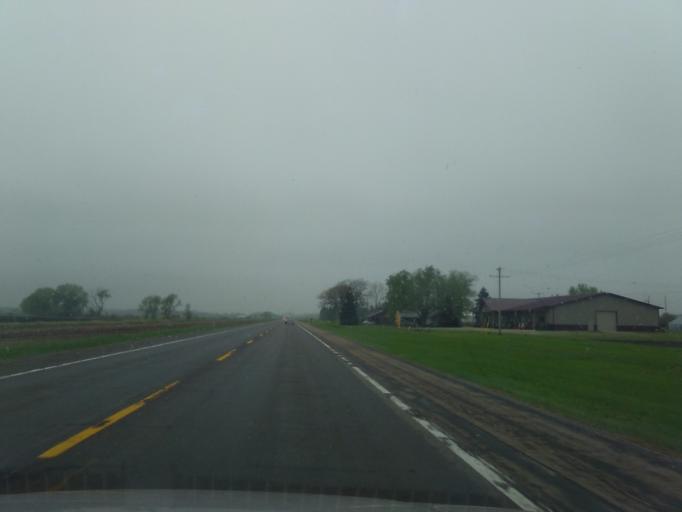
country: US
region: Nebraska
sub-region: Cuming County
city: West Point
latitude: 41.9135
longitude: -96.7855
